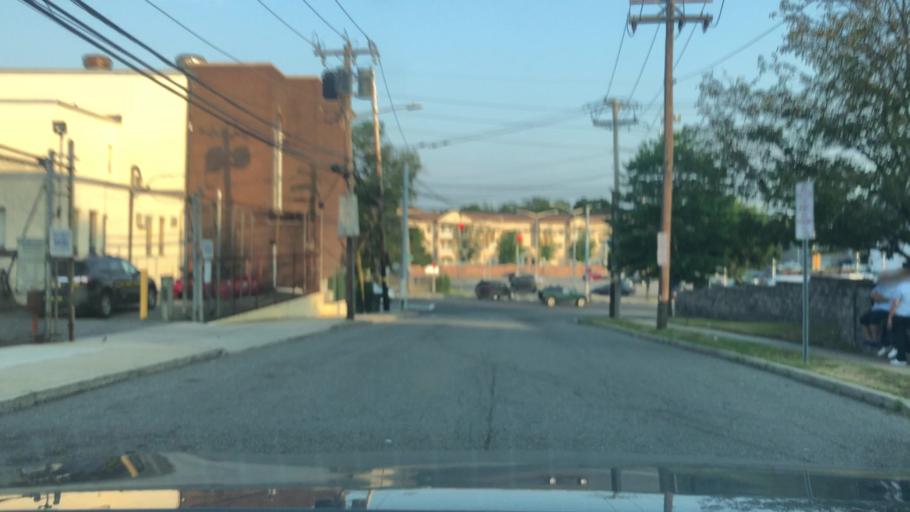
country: US
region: New York
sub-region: Nassau County
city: Elmont
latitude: 40.7067
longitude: -73.7090
